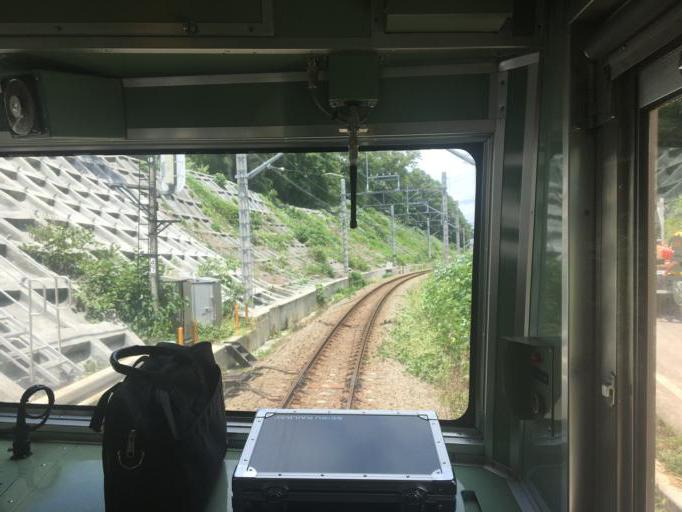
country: JP
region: Tokyo
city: Higashimurayama-shi
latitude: 35.7578
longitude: 139.4435
